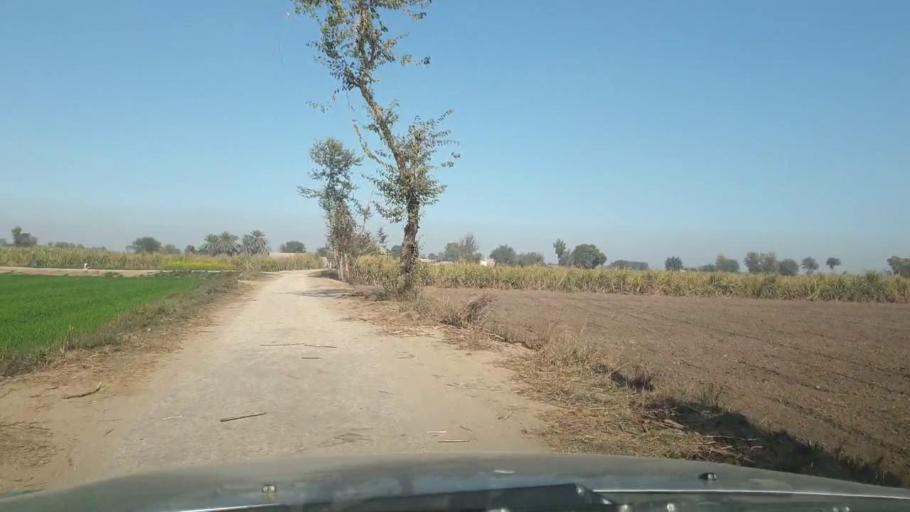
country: PK
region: Sindh
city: Ghotki
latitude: 28.0291
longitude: 69.2499
